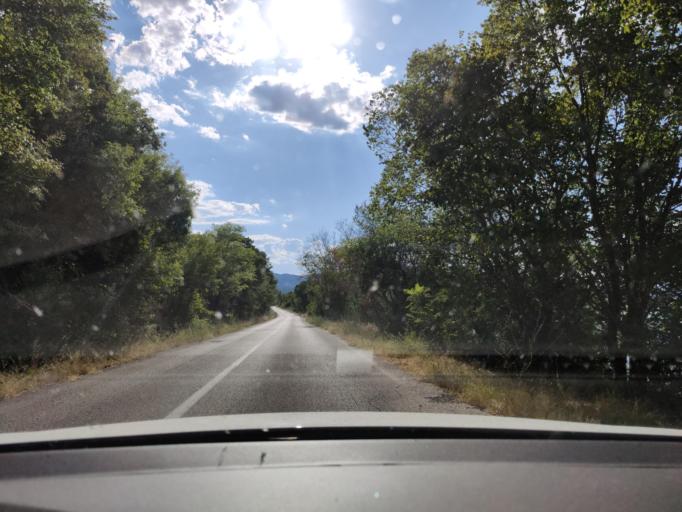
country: GR
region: Central Macedonia
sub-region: Nomos Serron
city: Chrysochorafa
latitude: 41.1790
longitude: 23.1345
